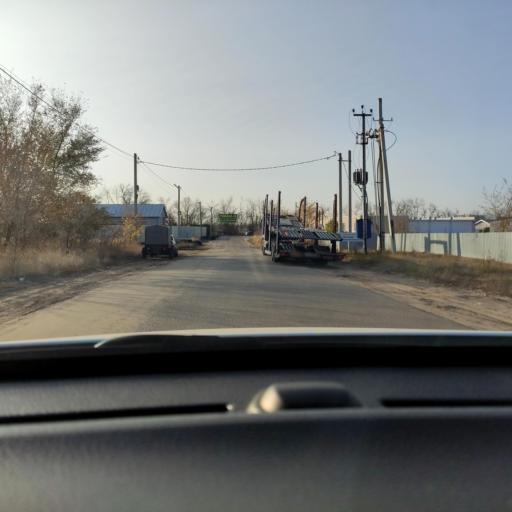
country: RU
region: Voronezj
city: Somovo
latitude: 51.6754
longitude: 39.3041
